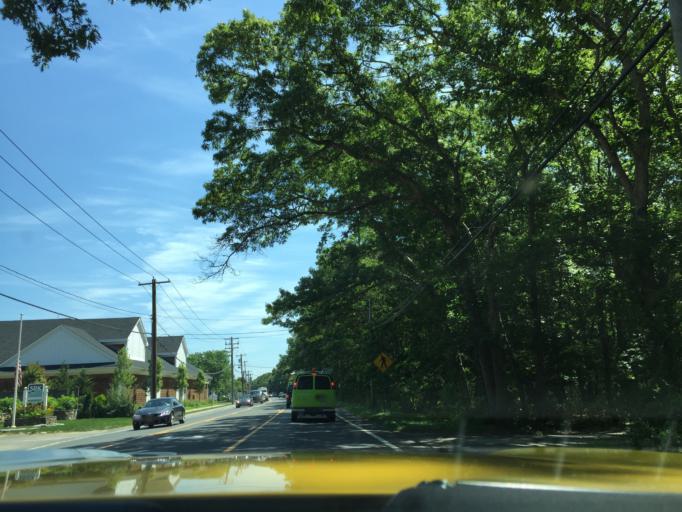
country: US
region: New York
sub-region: Suffolk County
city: Bridgehampton
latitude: 40.9471
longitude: -72.2500
